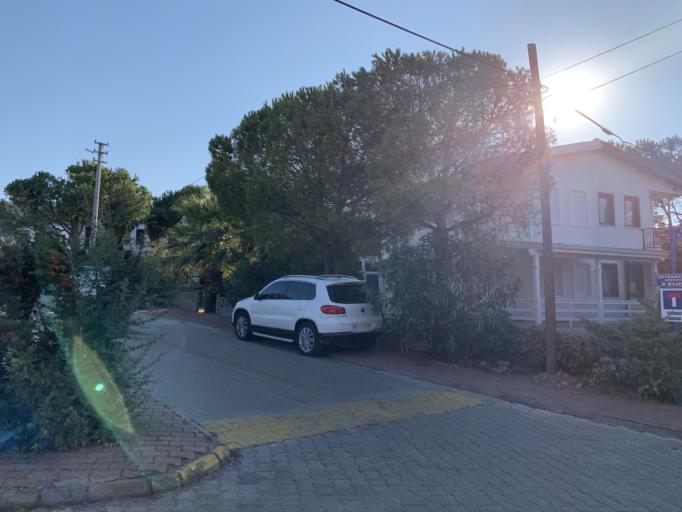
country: TR
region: Balikesir
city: Ayvalik
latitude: 39.3513
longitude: 26.6497
